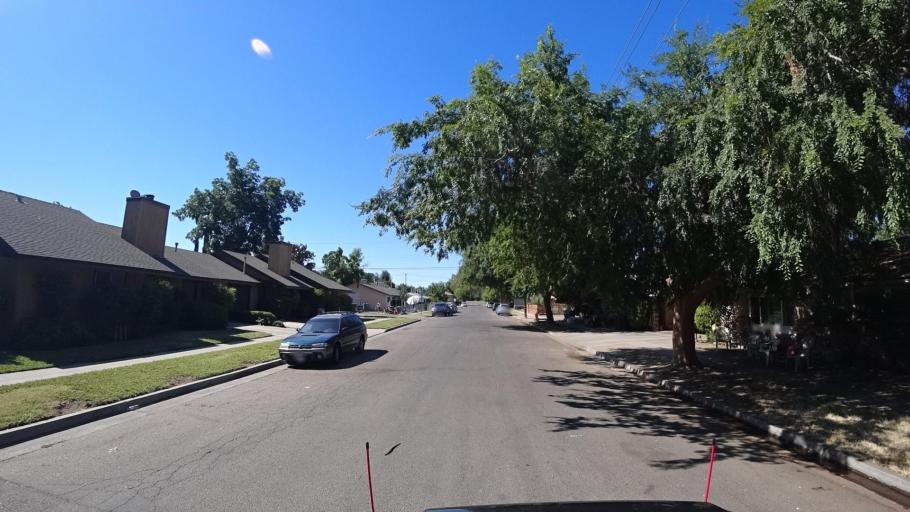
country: US
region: California
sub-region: Fresno County
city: Fresno
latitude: 36.7749
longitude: -119.7974
